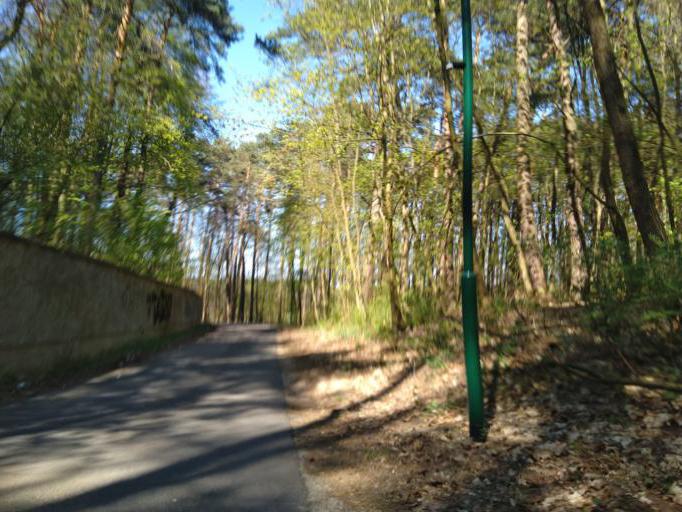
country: DE
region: Brandenburg
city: Biesenthal
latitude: 52.7715
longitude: 13.6042
